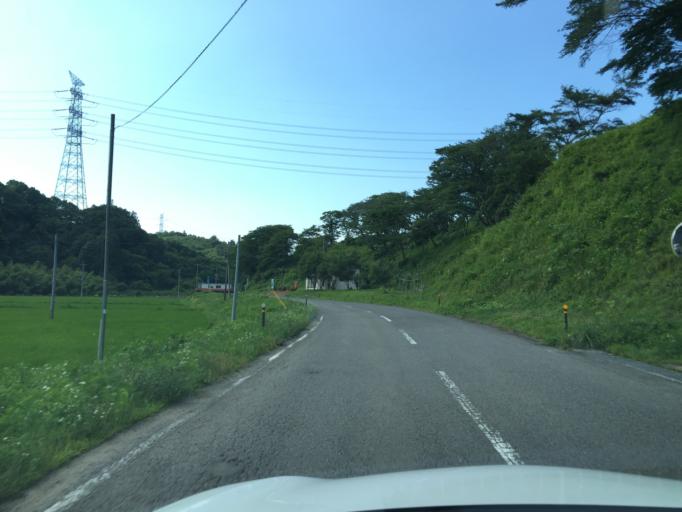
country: JP
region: Fukushima
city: Ishikawa
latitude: 37.1720
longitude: 140.6188
